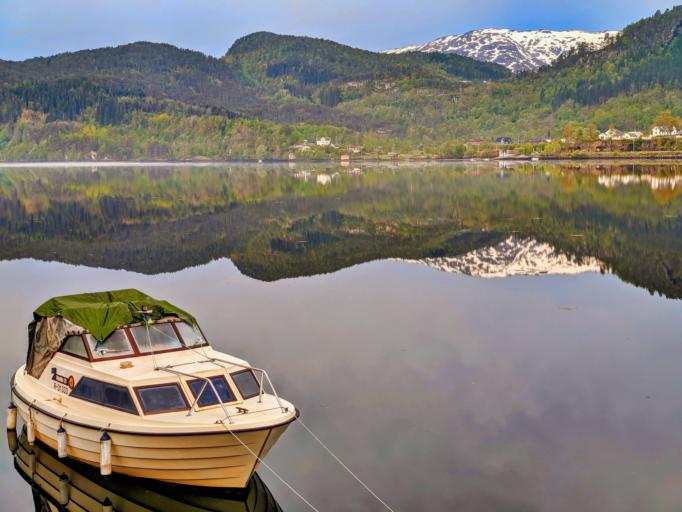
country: NO
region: Hordaland
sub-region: Samnanger
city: Tysse
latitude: 60.4026
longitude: 5.7286
